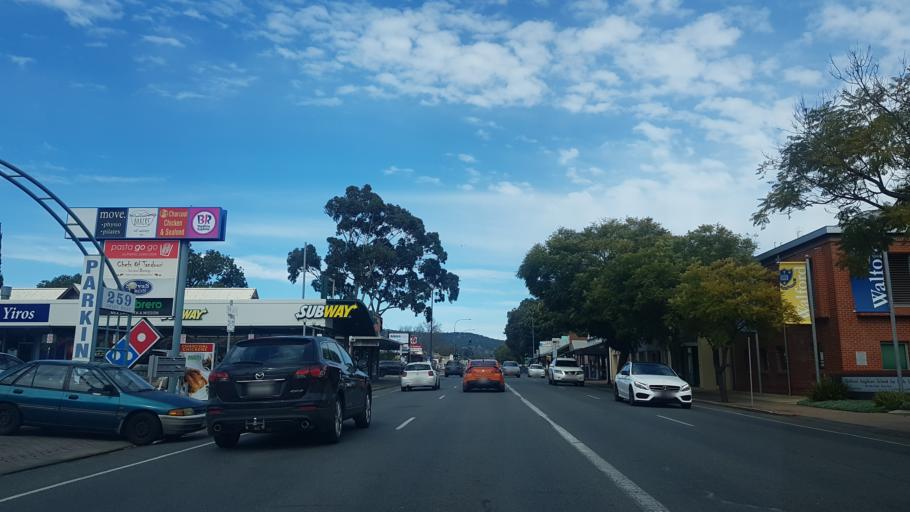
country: AU
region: South Australia
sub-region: Unley
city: Unley Park
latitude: -34.9570
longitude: 138.6081
